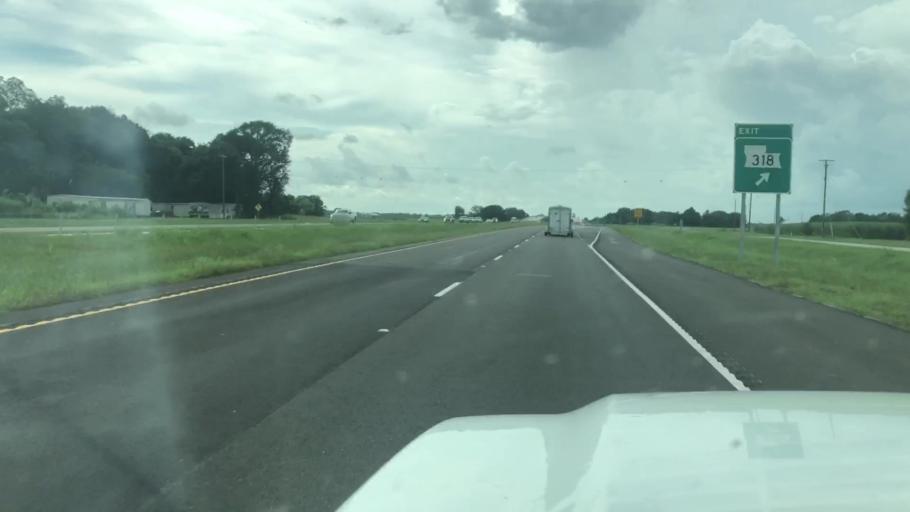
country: US
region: Louisiana
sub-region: Iberia Parish
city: Jeanerette
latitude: 29.8627
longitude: -91.6255
